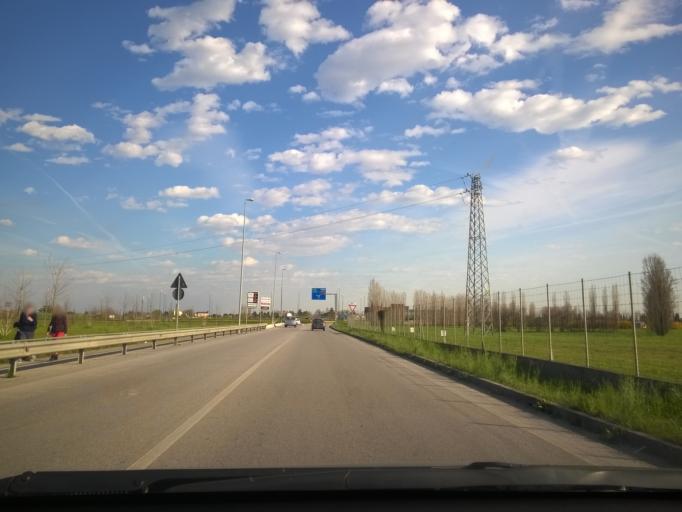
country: IT
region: Veneto
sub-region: Provincia di Treviso
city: Lancenigo-Villorba
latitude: 45.7414
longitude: 12.2565
